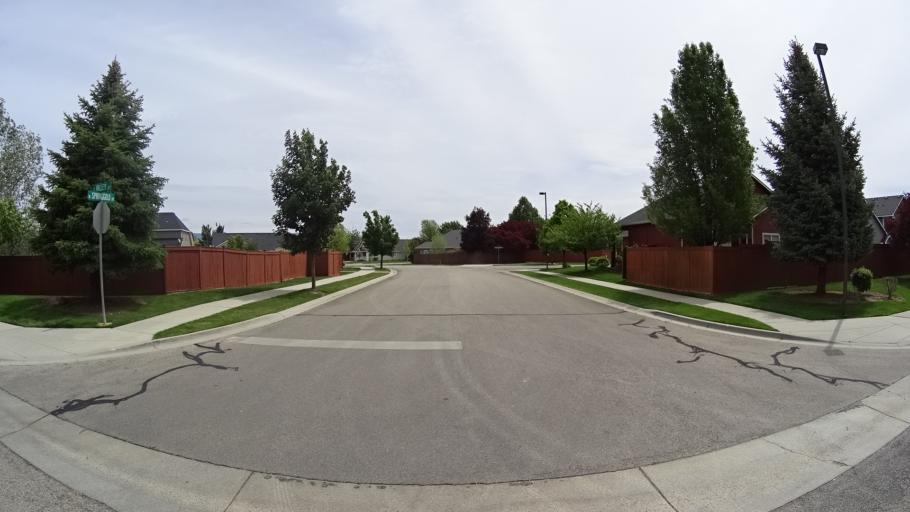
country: US
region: Idaho
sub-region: Ada County
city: Meridian
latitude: 43.5487
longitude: -116.3243
